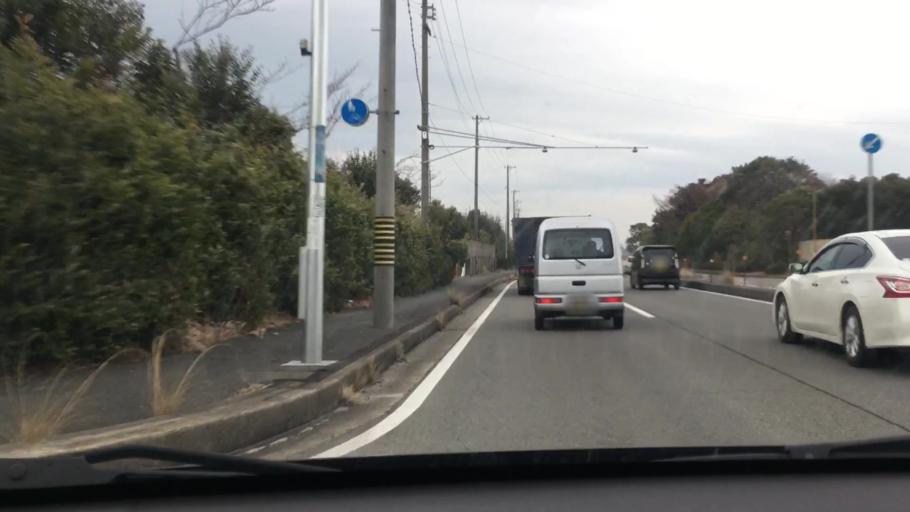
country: JP
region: Mie
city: Suzuka
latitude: 34.8829
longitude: 136.5259
